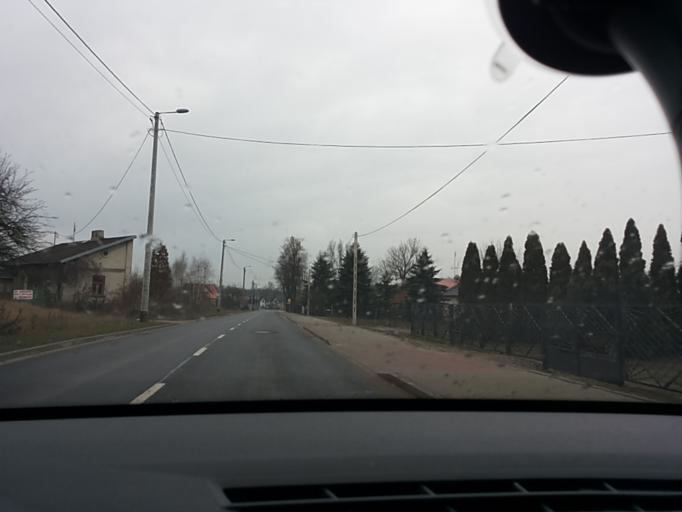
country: PL
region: Lodz Voivodeship
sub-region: Skierniewice
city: Skierniewice
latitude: 51.9710
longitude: 20.1305
